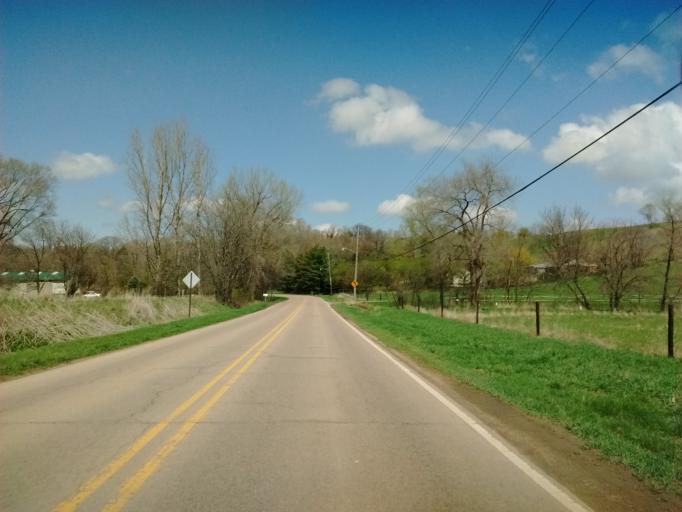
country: US
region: Iowa
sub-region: Woodbury County
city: Sioux City
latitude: 42.5415
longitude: -96.4306
